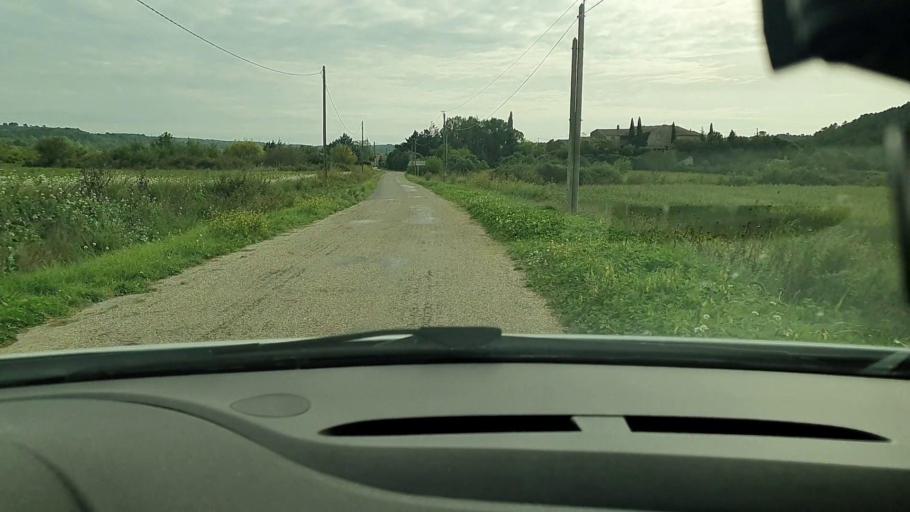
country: FR
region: Languedoc-Roussillon
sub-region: Departement du Gard
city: Montaren-et-Saint-Mediers
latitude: 44.0889
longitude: 4.3497
